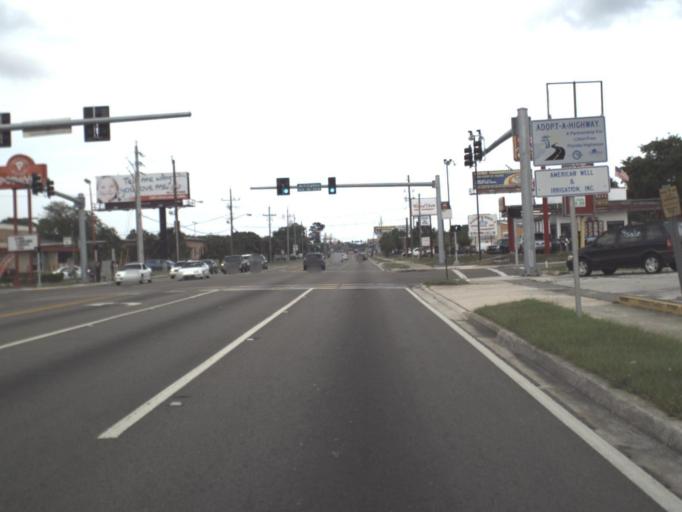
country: US
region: Florida
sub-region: Duval County
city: Jacksonville
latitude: 30.3133
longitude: -81.5797
